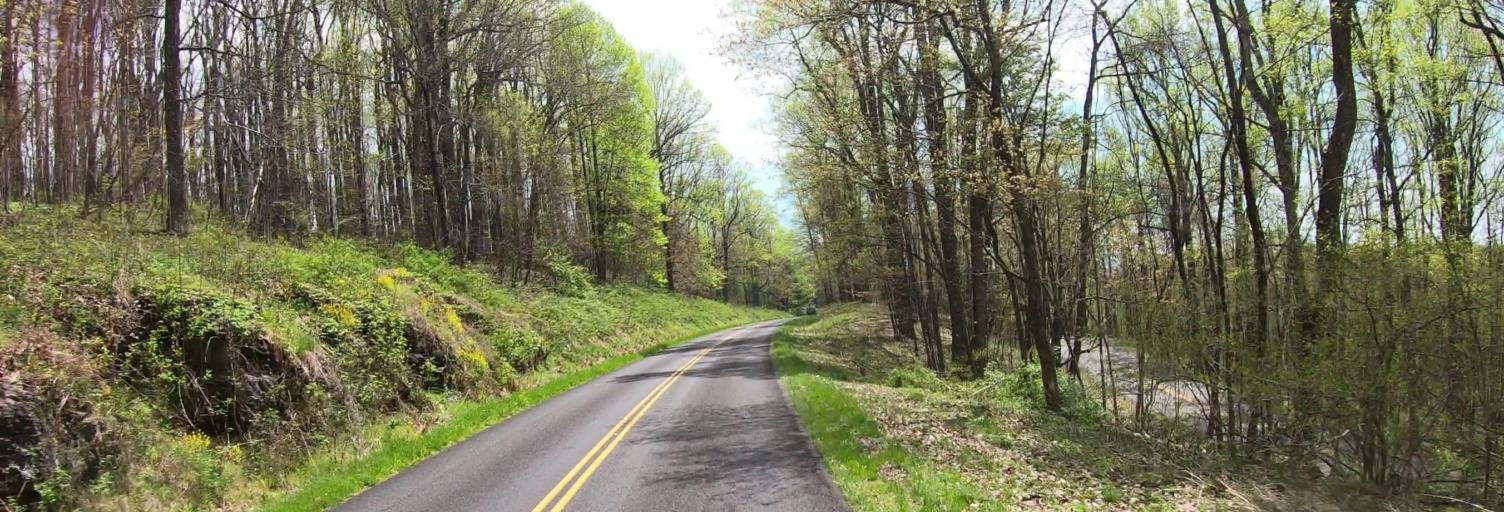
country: US
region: Virginia
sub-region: Carroll County
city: Cana
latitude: 36.6691
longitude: -80.6585
